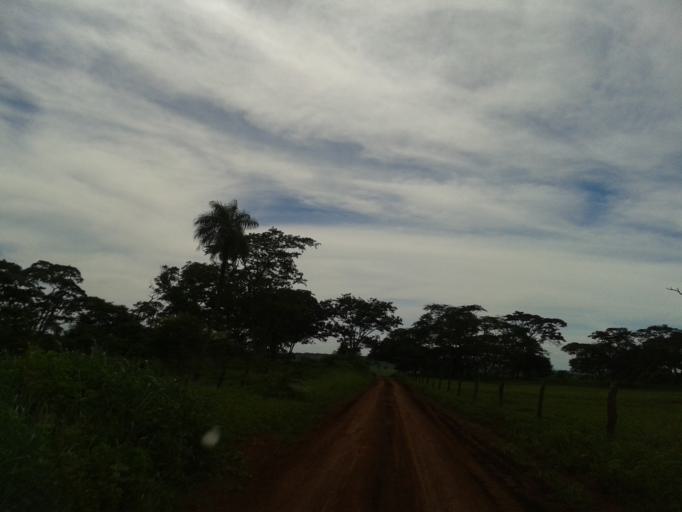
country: BR
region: Minas Gerais
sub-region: Capinopolis
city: Capinopolis
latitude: -18.7488
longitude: -49.8323
